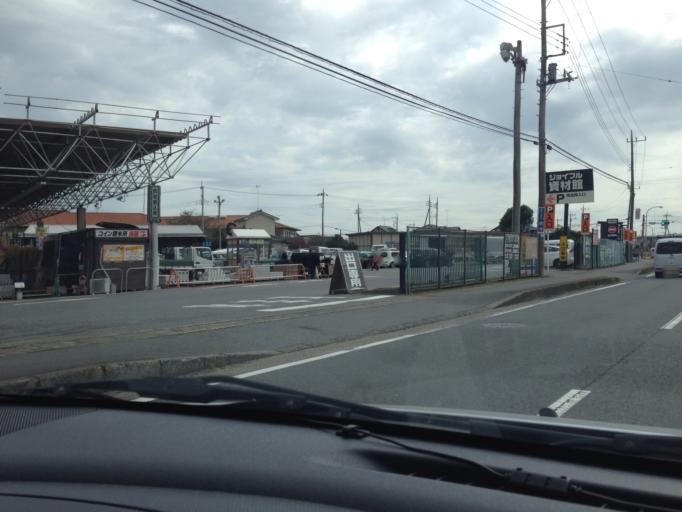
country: JP
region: Ibaraki
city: Naka
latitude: 36.0364
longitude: 140.1655
